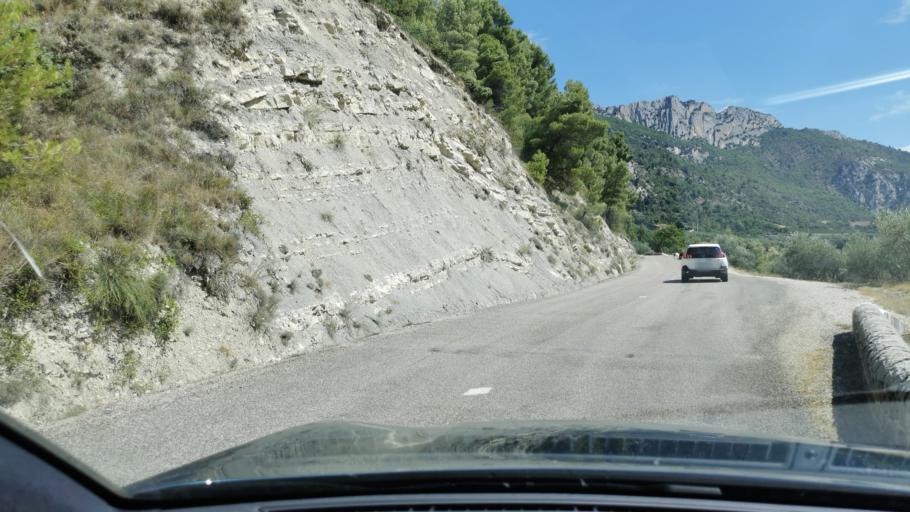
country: FR
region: Rhone-Alpes
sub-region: Departement de la Drome
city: Buis-les-Baronnies
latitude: 44.2981
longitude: 5.2843
